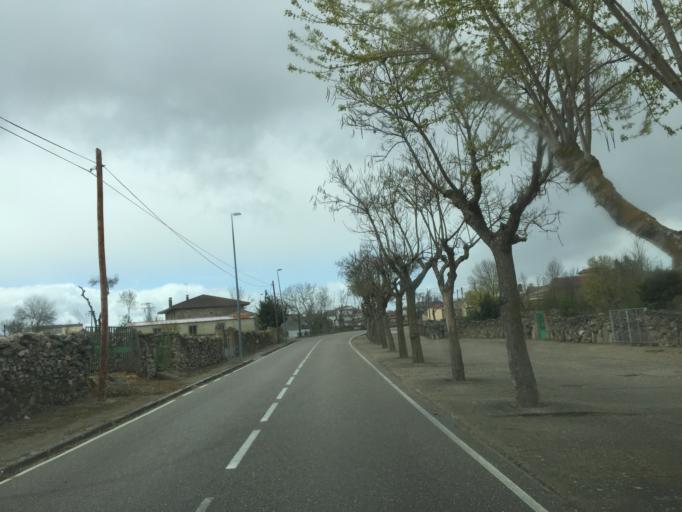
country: ES
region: Castille and Leon
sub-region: Provincia de Zamora
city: Villalcampo
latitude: 41.5223
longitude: -6.0451
